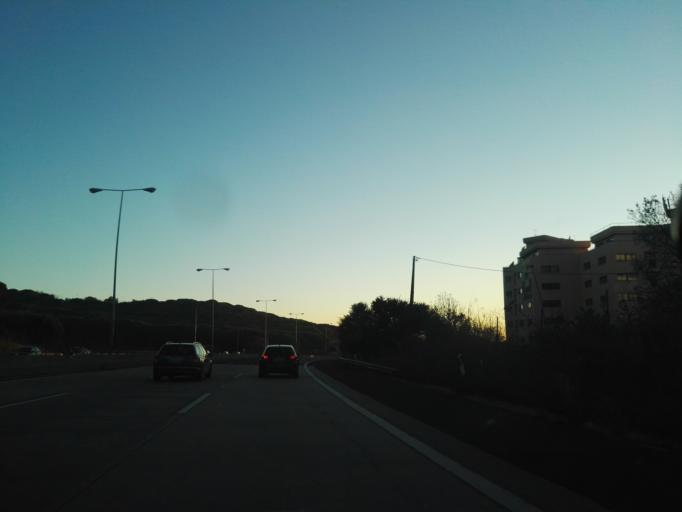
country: PT
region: Lisbon
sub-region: Oeiras
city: Alges
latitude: 38.7082
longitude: -9.2224
